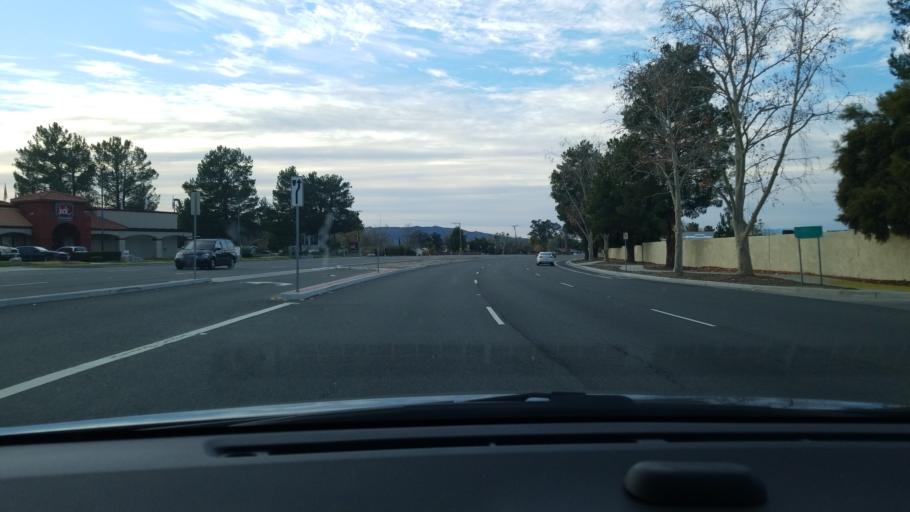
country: US
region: California
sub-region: Riverside County
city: San Jacinto
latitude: 33.8021
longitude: -116.9732
